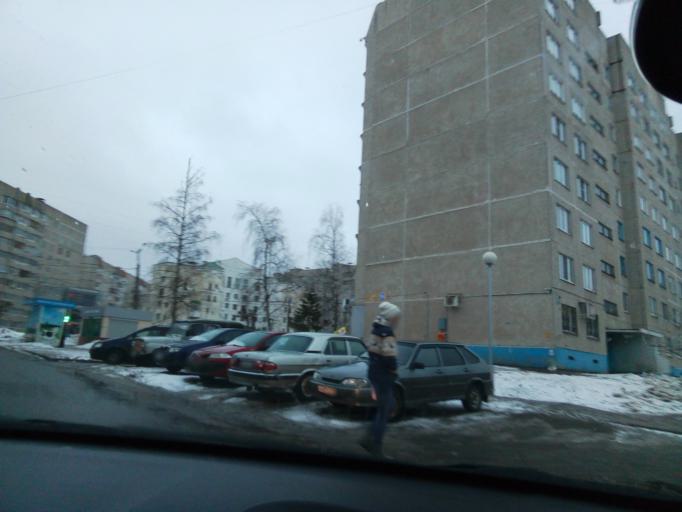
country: RU
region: Chuvashia
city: Novyye Lapsary
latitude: 56.1143
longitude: 47.1863
